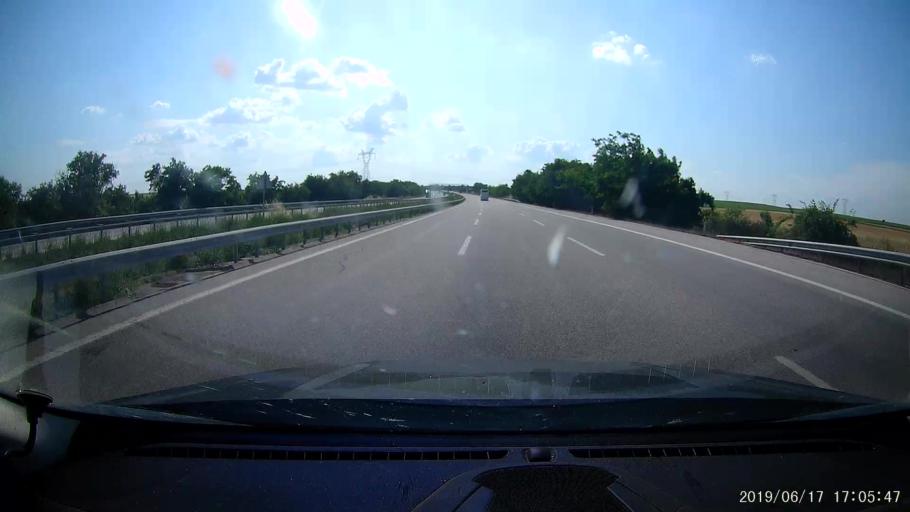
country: TR
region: Edirne
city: Edirne
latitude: 41.6618
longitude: 26.6896
